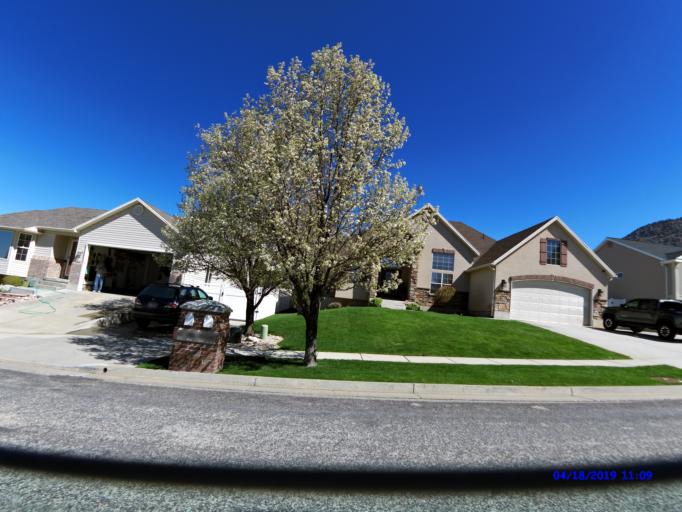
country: US
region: Utah
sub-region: Weber County
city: North Ogden
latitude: 41.2824
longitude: -111.9503
